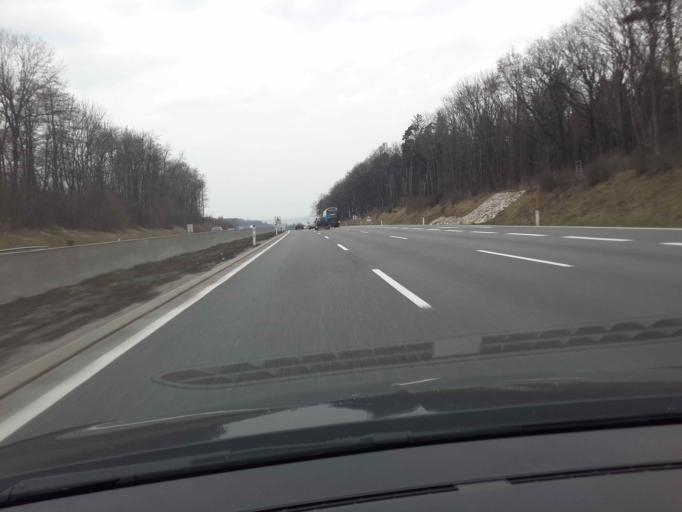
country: AT
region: Lower Austria
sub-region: Politischer Bezirk Sankt Polten
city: Kirchstetten
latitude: 48.1758
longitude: 15.8386
